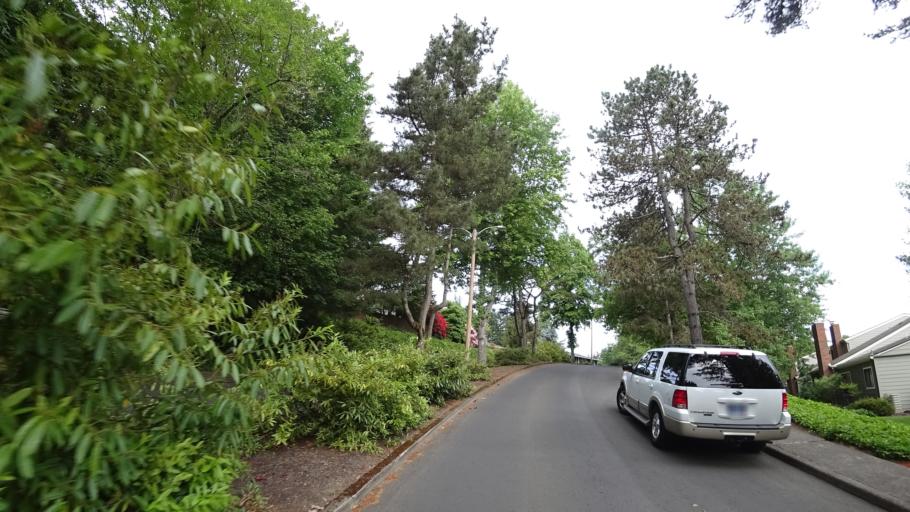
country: US
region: Oregon
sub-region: Clackamas County
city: Lake Oswego
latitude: 45.4304
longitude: -122.6815
